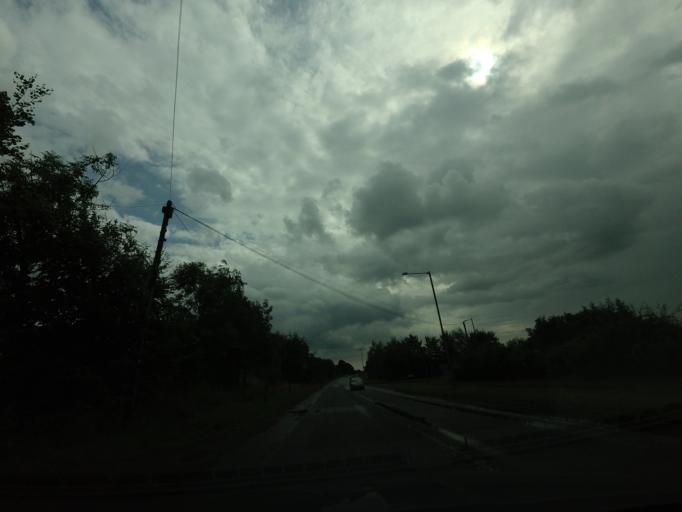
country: GB
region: Scotland
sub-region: Dumfries and Galloway
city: Lockerbie
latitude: 55.1330
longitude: -3.3636
